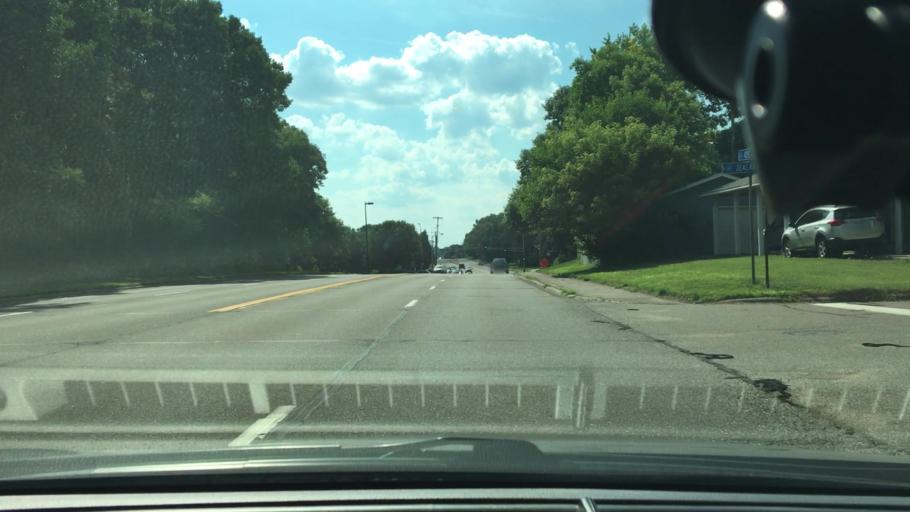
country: US
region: Minnesota
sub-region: Hennepin County
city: New Hope
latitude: 45.0331
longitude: -93.3879
